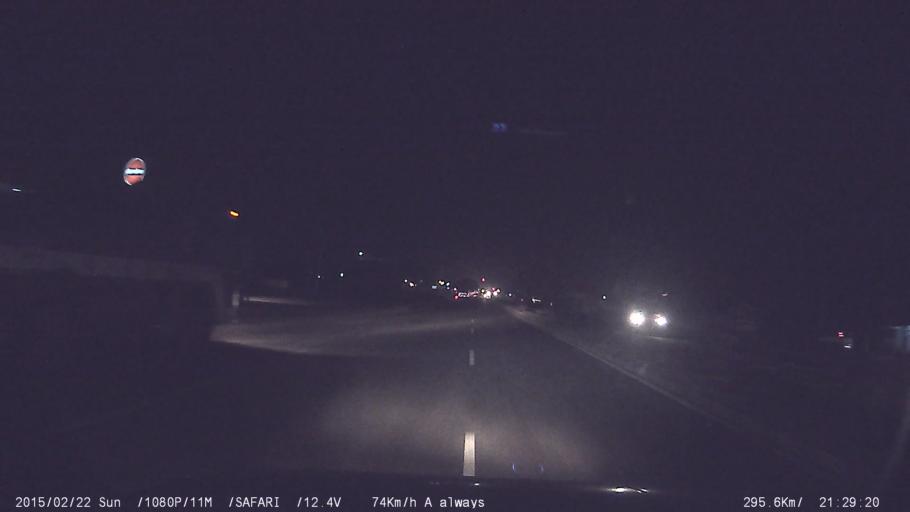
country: IN
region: Tamil Nadu
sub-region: Karur
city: Karur
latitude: 10.9329
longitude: 78.0549
